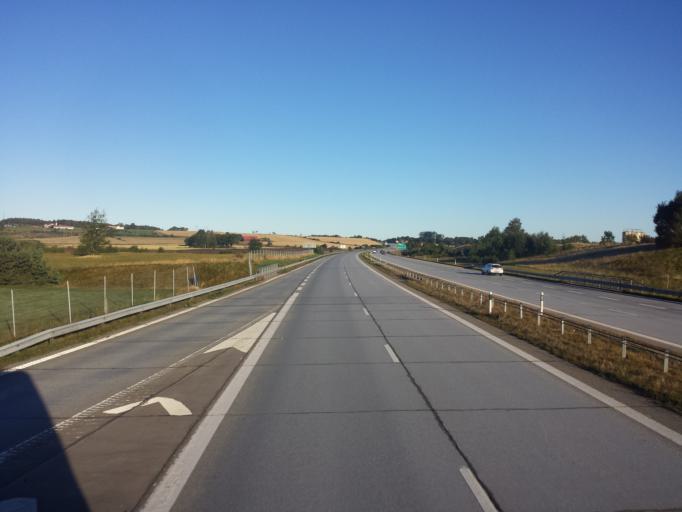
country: SE
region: Halland
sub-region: Falkenbergs Kommun
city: Falkenberg
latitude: 56.8864
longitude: 12.6034
